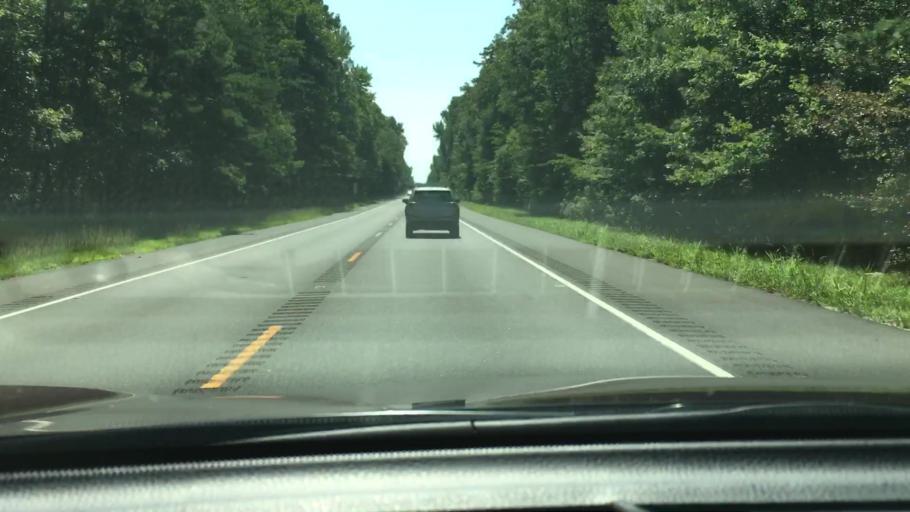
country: US
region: New Jersey
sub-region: Cape May County
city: Woodbine
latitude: 39.3341
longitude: -74.8816
